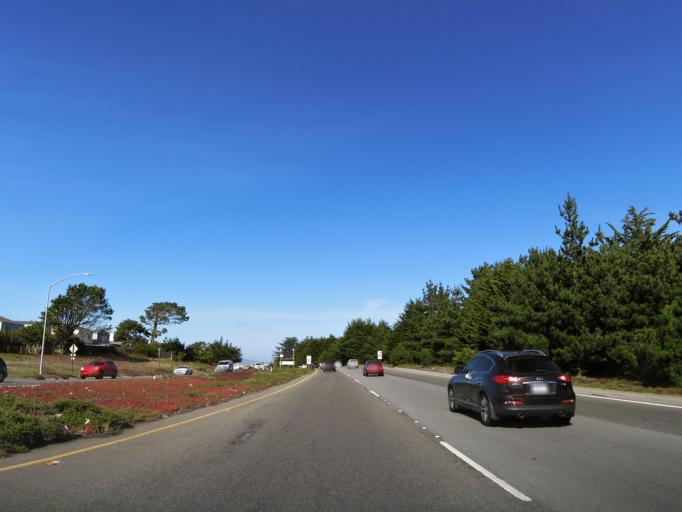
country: US
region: California
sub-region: San Mateo County
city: Broadmoor
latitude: 37.6835
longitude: -122.4891
